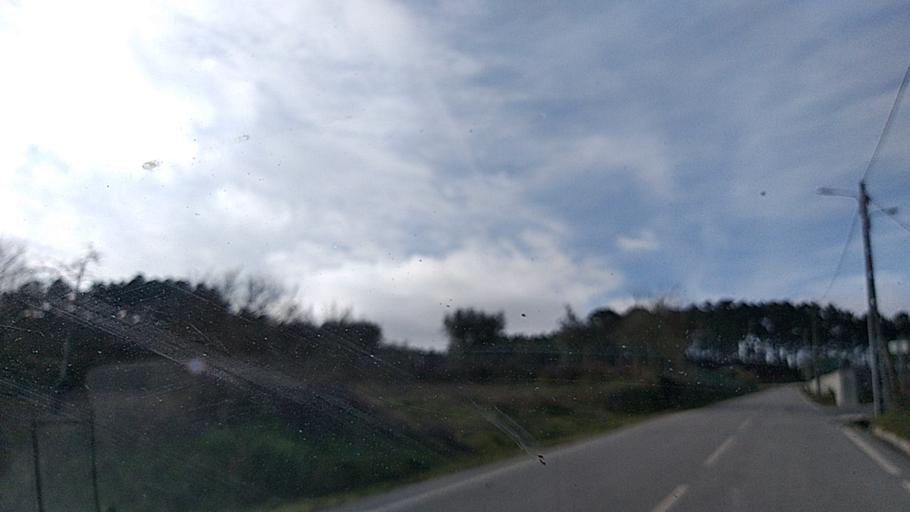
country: PT
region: Guarda
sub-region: Fornos de Algodres
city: Fornos de Algodres
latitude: 40.7011
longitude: -7.5605
